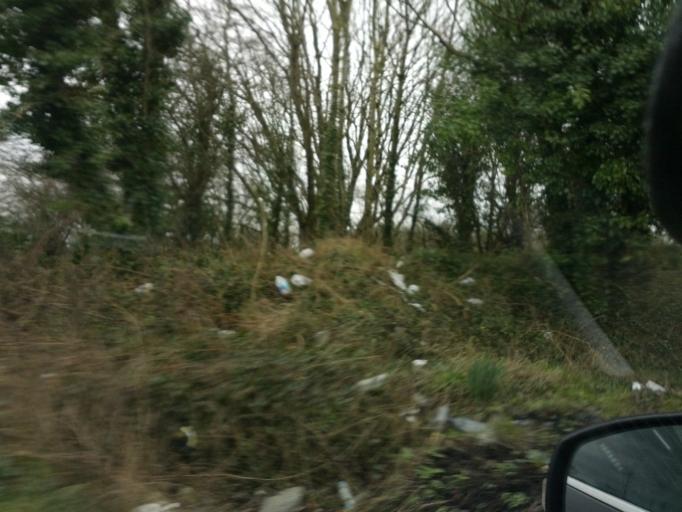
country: IE
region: Connaught
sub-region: County Galway
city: Athenry
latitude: 53.2542
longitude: -8.7442
